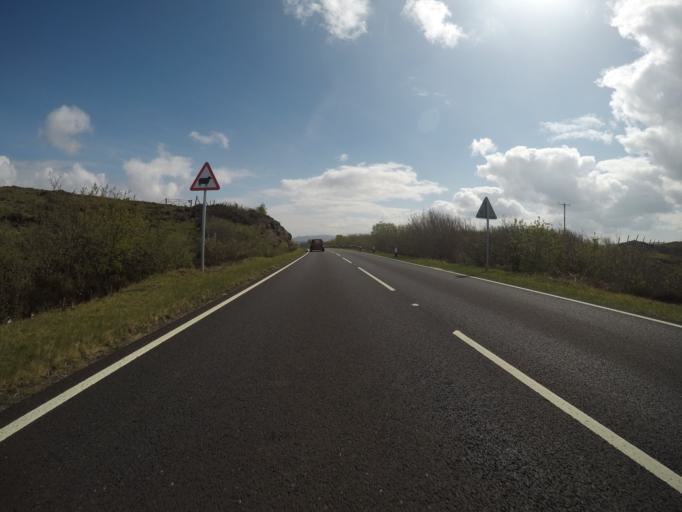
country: GB
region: Scotland
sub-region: Highland
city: Portree
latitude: 57.5017
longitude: -6.3292
